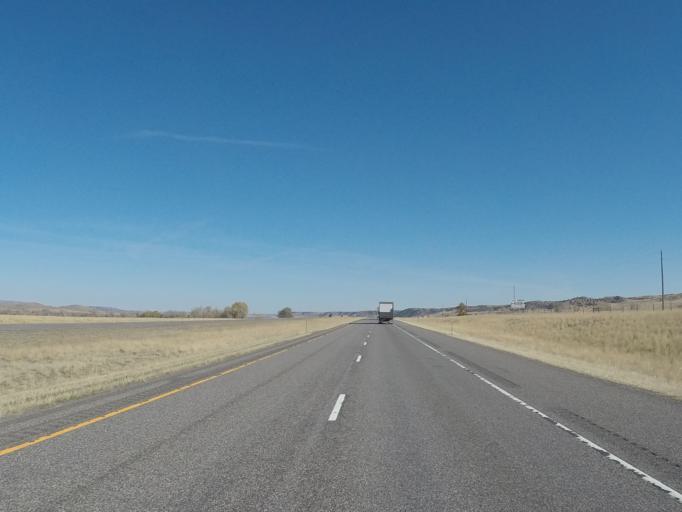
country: US
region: Montana
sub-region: Sweet Grass County
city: Big Timber
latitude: 45.7496
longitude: -110.1645
